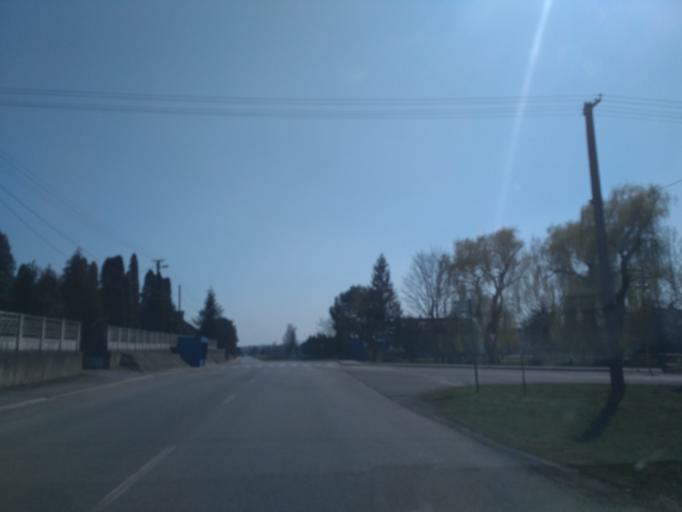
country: SK
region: Kosicky
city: Secovce
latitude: 48.6642
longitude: 21.6113
